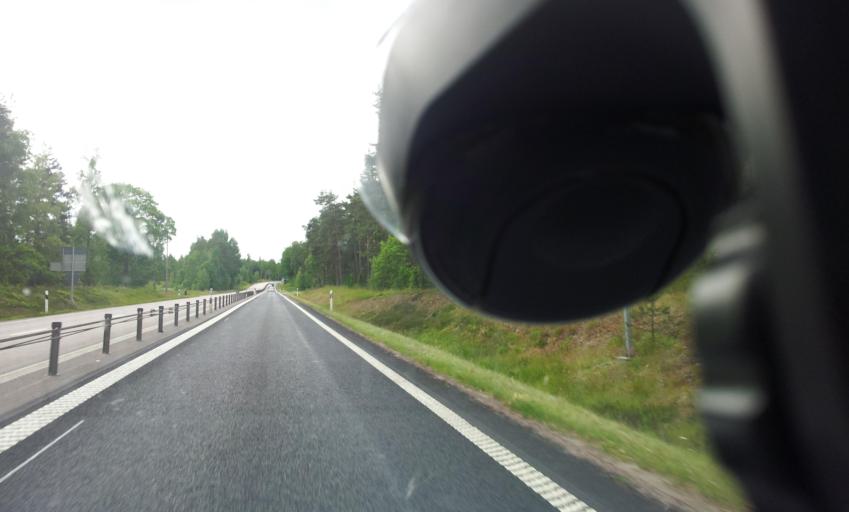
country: SE
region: Kalmar
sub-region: Oskarshamns Kommun
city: Oskarshamn
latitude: 57.3493
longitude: 16.4905
